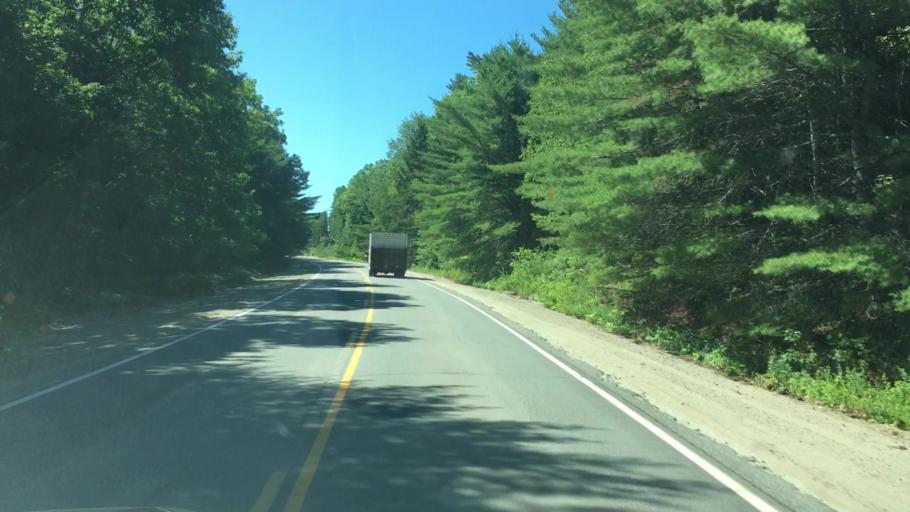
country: US
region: Maine
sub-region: Hancock County
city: Sedgwick
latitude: 44.3770
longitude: -68.5684
